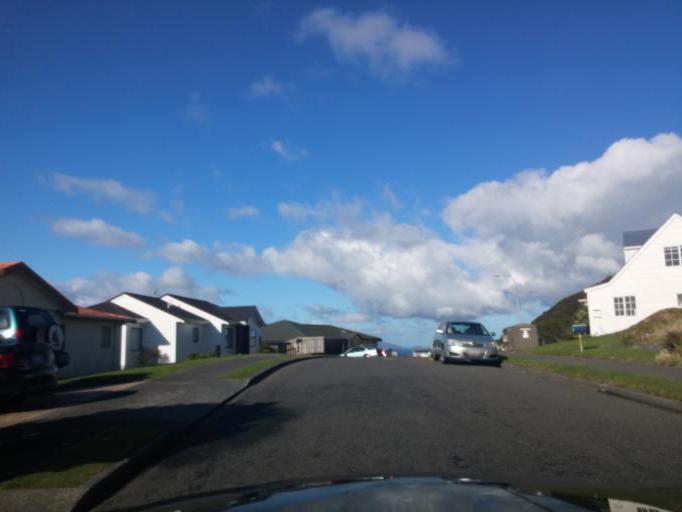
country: NZ
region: Wellington
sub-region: Wellington City
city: Wellington
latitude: -41.2335
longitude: 174.7913
